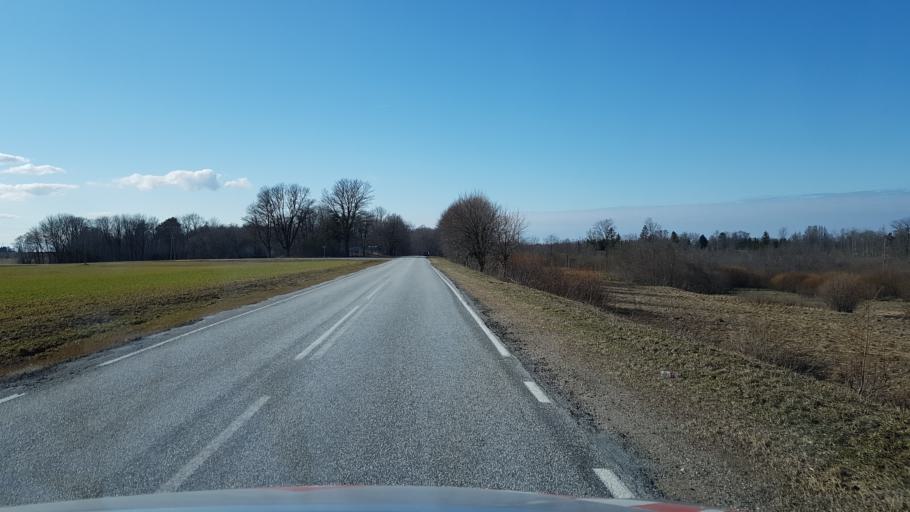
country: EE
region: Laeaene-Virumaa
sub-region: Haljala vald
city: Haljala
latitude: 59.4745
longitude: 26.1653
